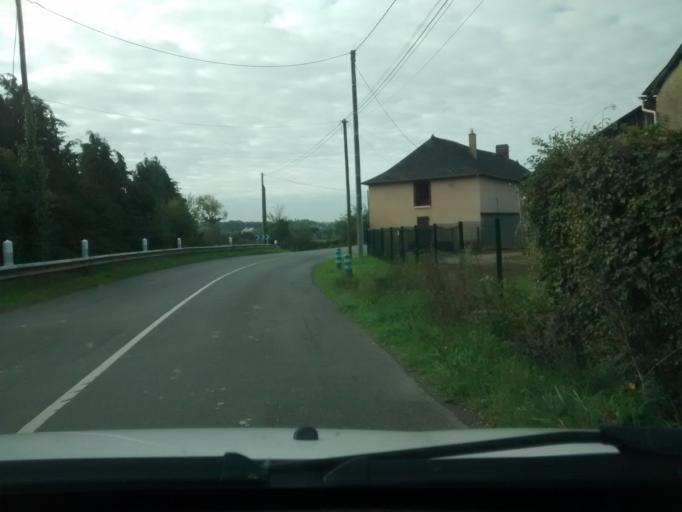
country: FR
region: Brittany
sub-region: Departement d'Ille-et-Vilaine
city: Vezin-le-Coquet
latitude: 48.0814
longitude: -1.7565
